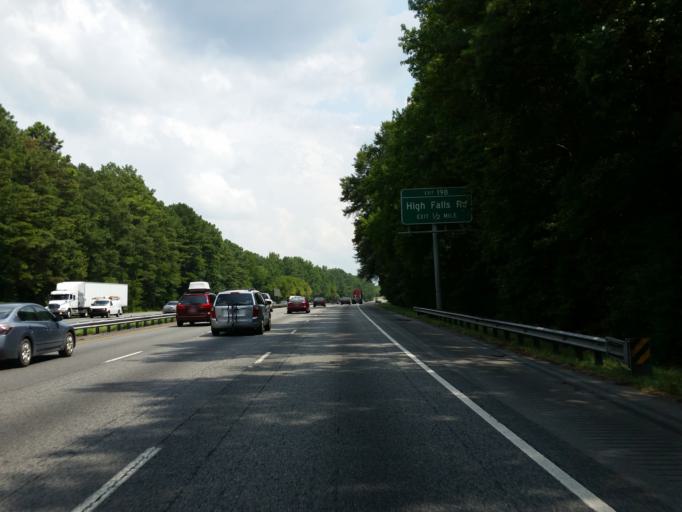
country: US
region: Georgia
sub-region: Butts County
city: Indian Springs
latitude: 33.1766
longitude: -84.0460
